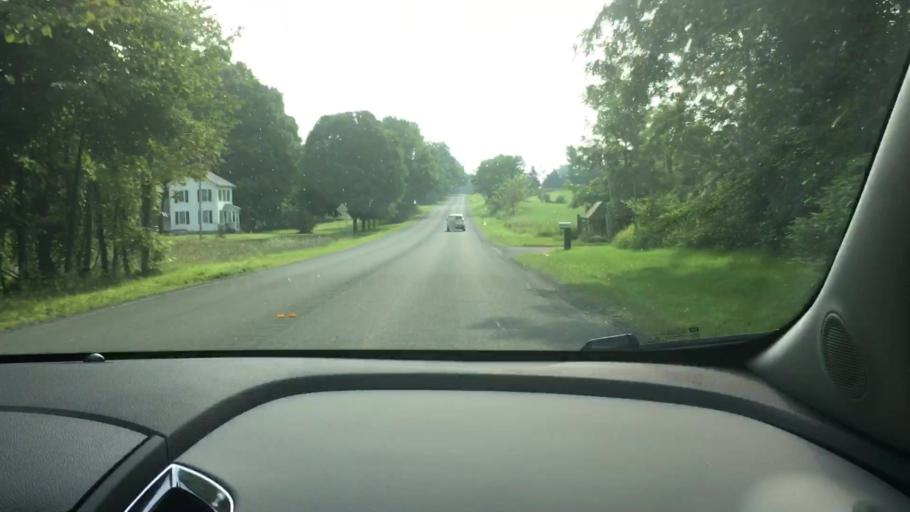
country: US
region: Michigan
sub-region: Kalamazoo County
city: Schoolcraft
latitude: 42.0273
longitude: -85.7022
